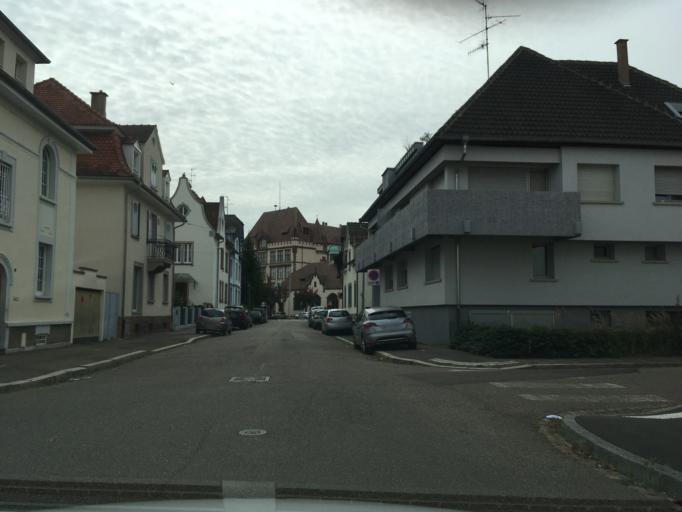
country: FR
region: Alsace
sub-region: Departement du Bas-Rhin
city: Bischheim
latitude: 48.6046
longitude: 7.7823
